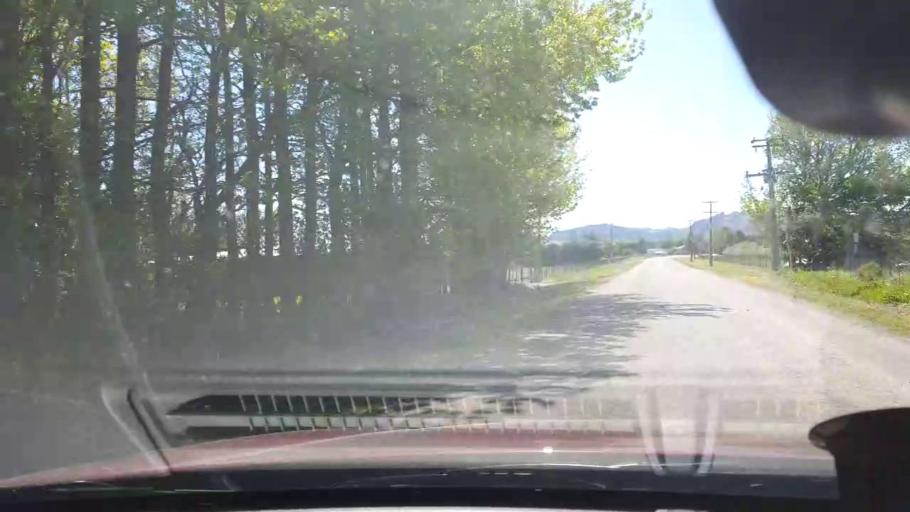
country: NZ
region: Gisborne
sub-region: Gisborne District
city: Gisborne
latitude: -38.6383
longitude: 177.9396
